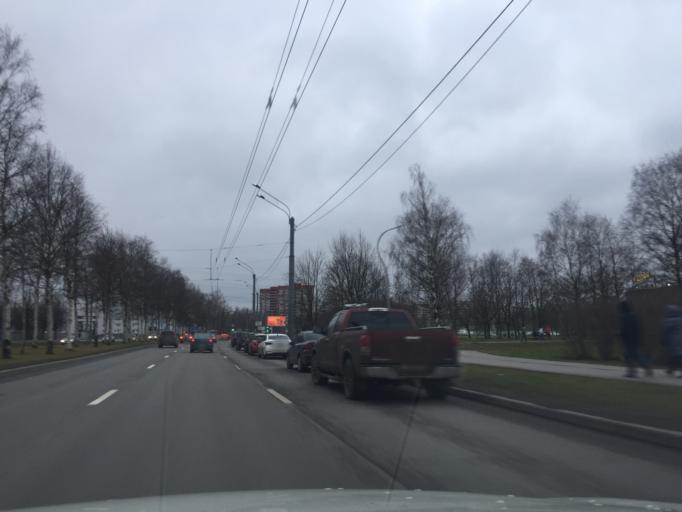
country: RU
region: Leningrad
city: Akademicheskoe
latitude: 60.0293
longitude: 30.3899
